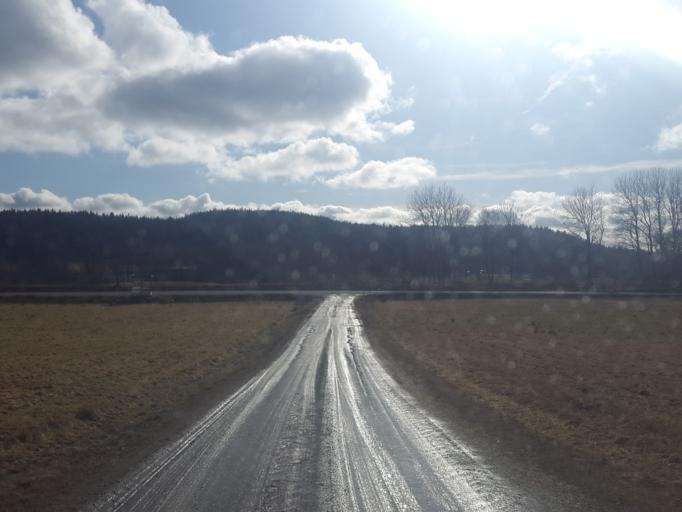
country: SE
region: Vaestra Goetaland
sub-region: Lerums Kommun
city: Olstorp
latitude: 57.8271
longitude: 12.2219
